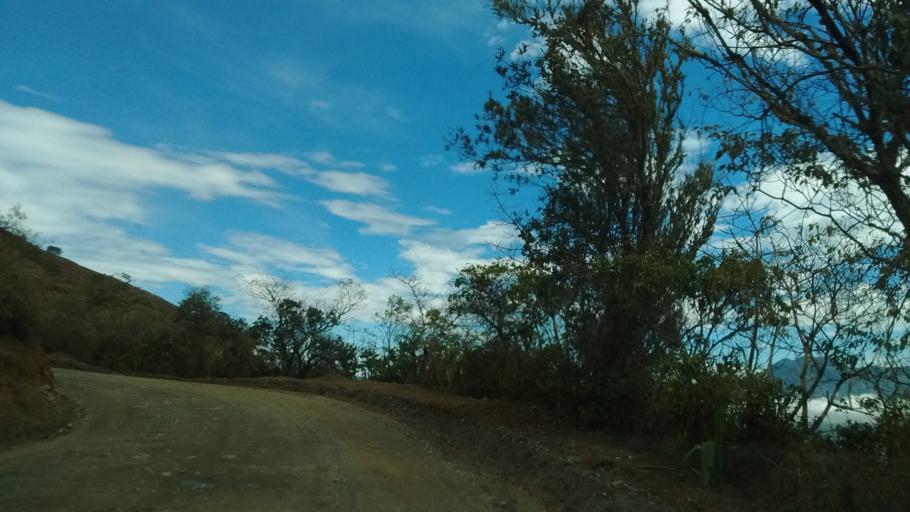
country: CO
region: Cauca
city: Almaguer
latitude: 1.8605
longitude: -76.9296
